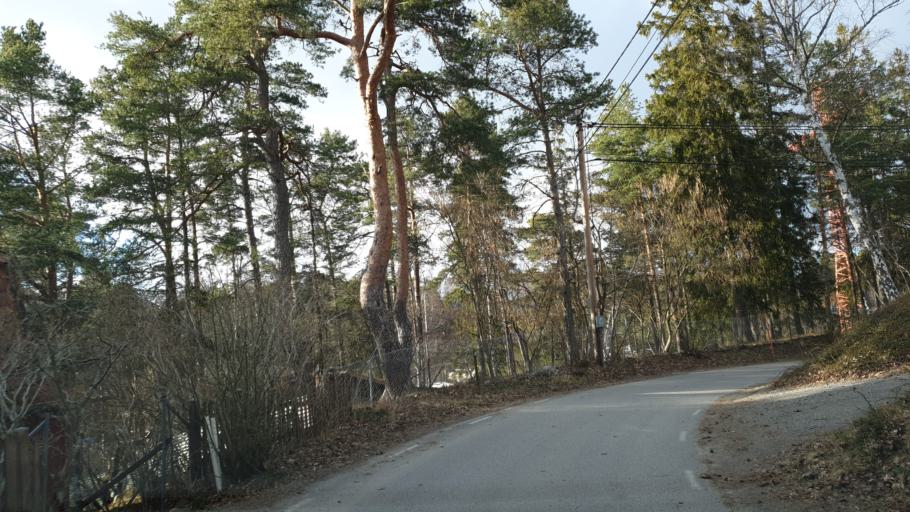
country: SE
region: Stockholm
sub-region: Varmdo Kommun
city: Holo
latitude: 59.3060
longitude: 18.6884
